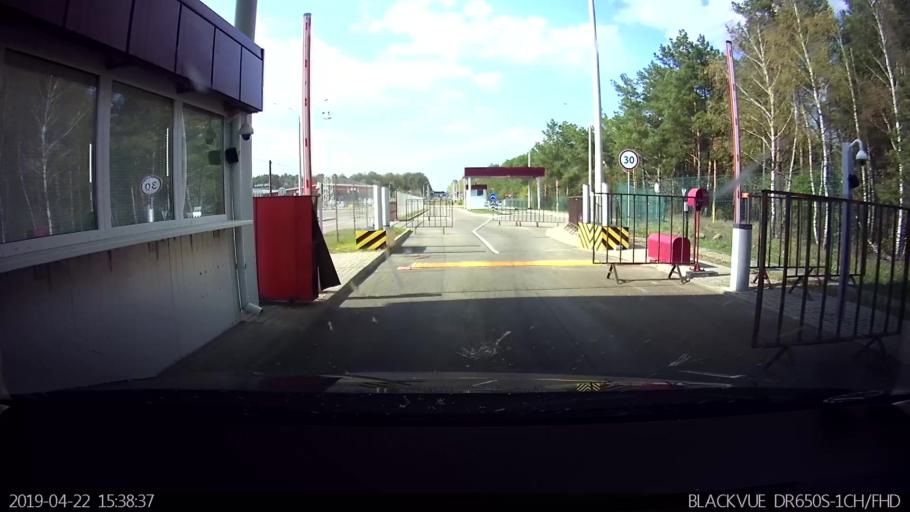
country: PL
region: Podlasie
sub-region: Powiat hajnowski
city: Czeremcha
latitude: 52.4650
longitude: 23.3613
